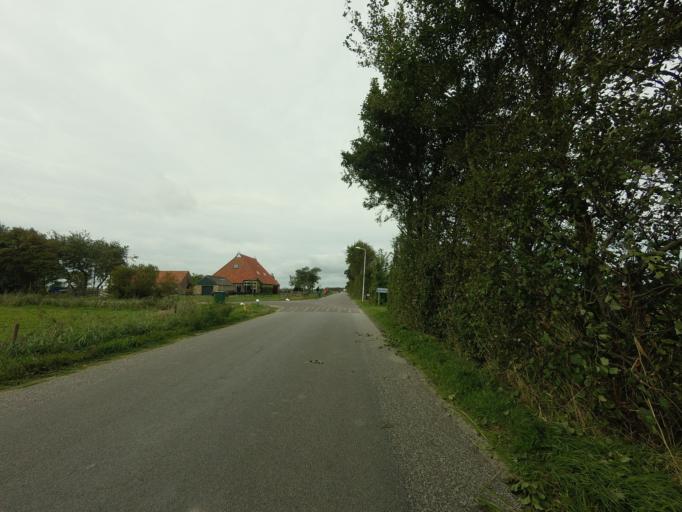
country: NL
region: Friesland
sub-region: Gemeente Ameland
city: Nes
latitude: 53.4405
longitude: 5.7082
